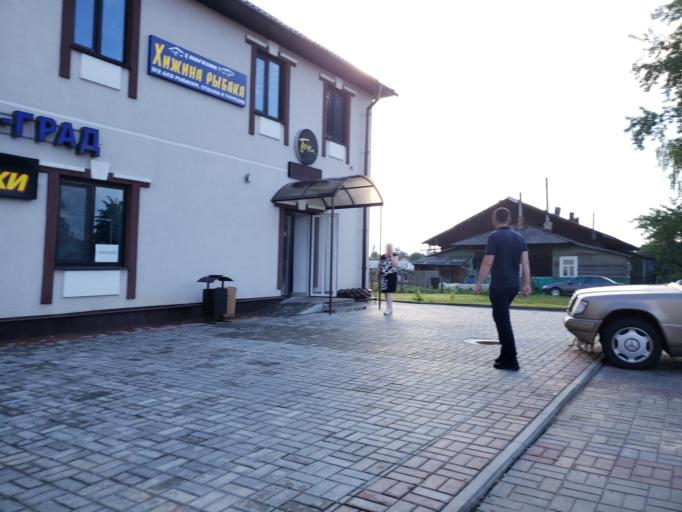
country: BY
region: Minsk
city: Chervyen'
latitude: 53.7057
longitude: 28.4345
